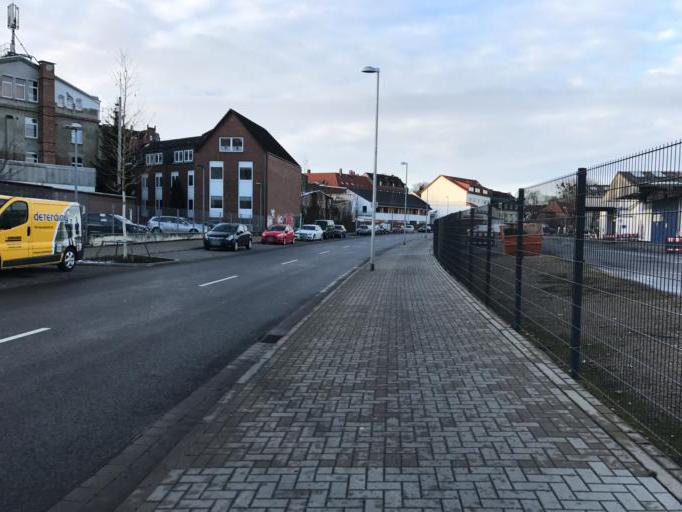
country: DE
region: Lower Saxony
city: Hannover
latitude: 52.3667
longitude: 9.7617
